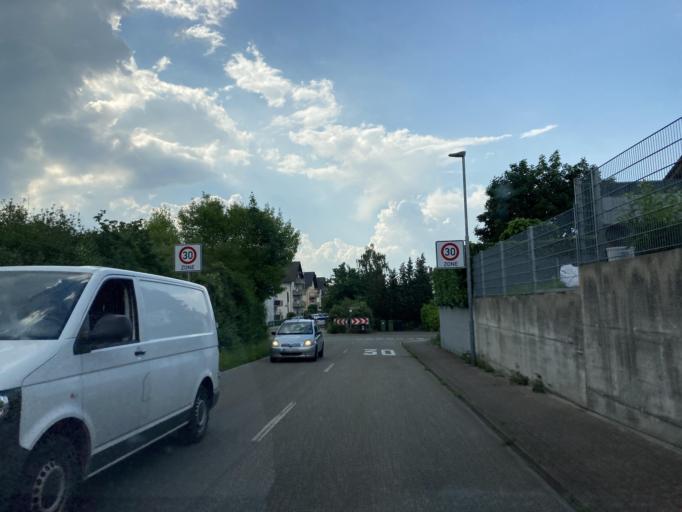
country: DE
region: Baden-Wuerttemberg
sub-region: Karlsruhe Region
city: Linkenheim-Hochstetten
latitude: 49.1310
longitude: 8.4139
